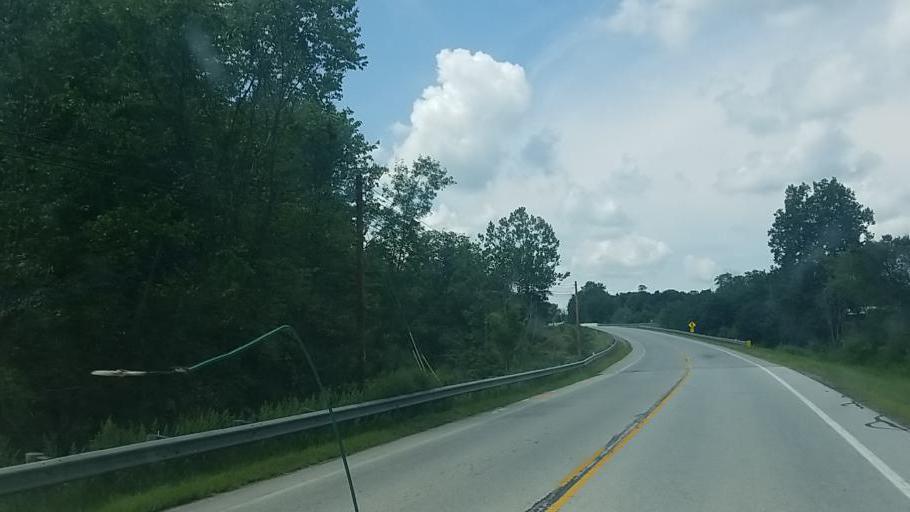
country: US
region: Ohio
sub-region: Wayne County
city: West Salem
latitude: 41.0275
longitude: -82.0925
